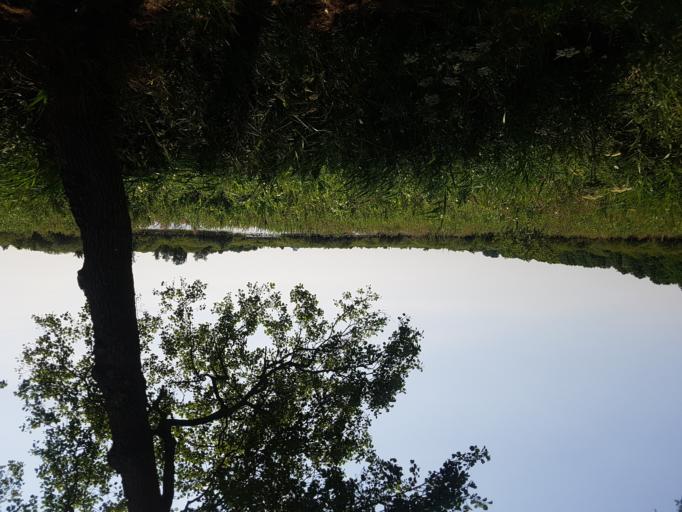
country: NL
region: Overijssel
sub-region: Gemeente Steenwijkerland
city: Tuk
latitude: 52.7698
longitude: 6.0887
